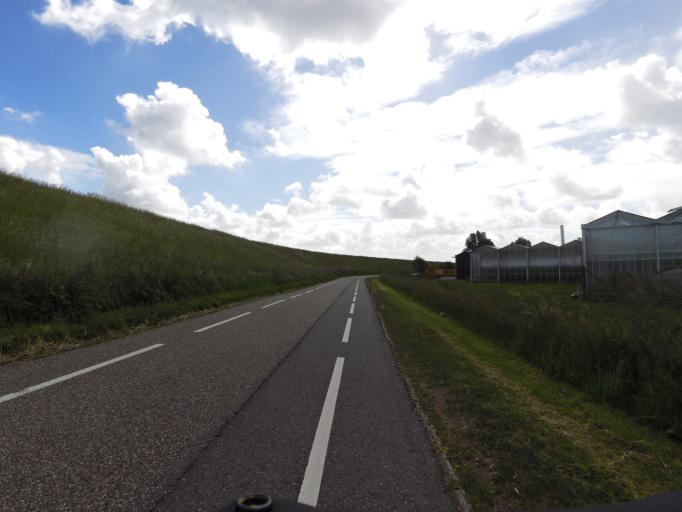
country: NL
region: Zeeland
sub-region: Schouwen-Duiveland
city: Bruinisse
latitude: 51.6811
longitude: 4.0521
